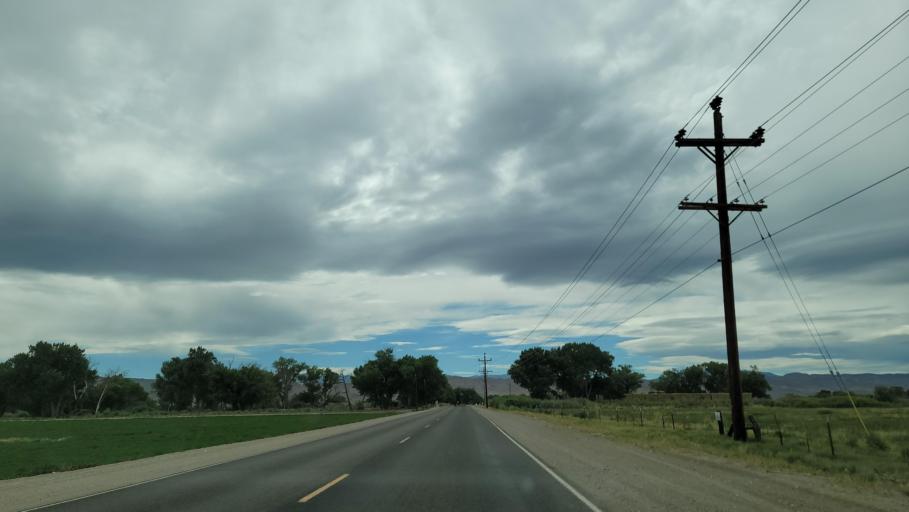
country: US
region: Nevada
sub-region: Lyon County
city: Yerington
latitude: 39.0482
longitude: -119.1601
